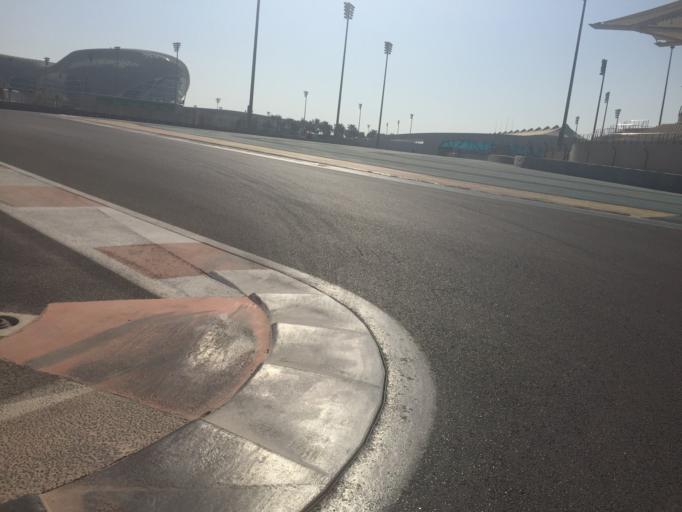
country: AE
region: Abu Dhabi
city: Abu Dhabi
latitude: 24.4686
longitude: 54.6016
